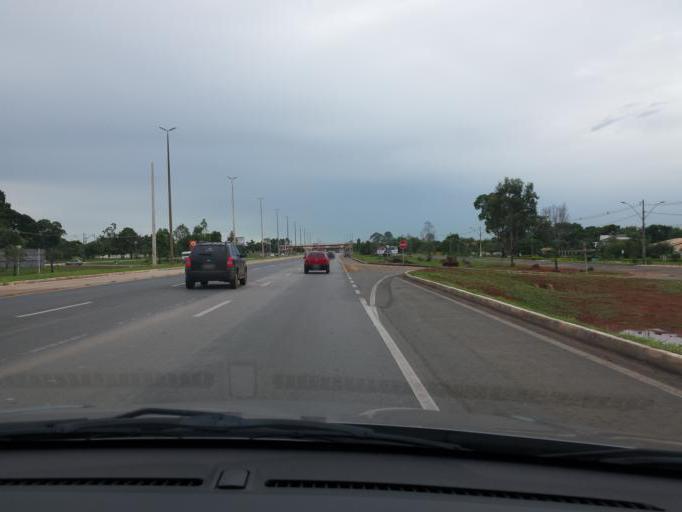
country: BR
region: Federal District
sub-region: Brasilia
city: Brasilia
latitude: -15.9154
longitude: -47.9702
